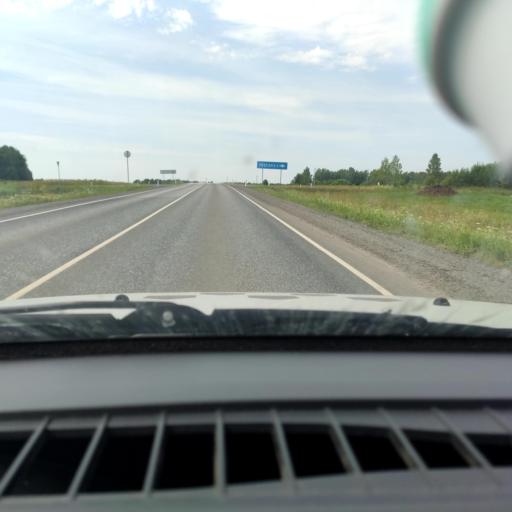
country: RU
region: Perm
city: Siva
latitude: 58.5220
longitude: 54.0036
